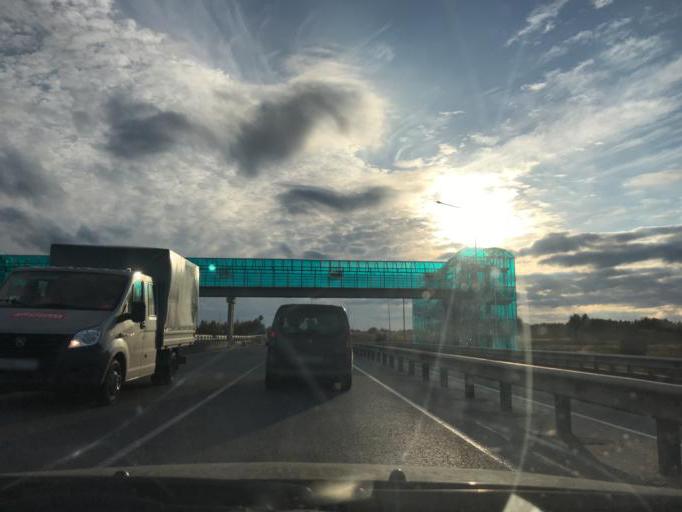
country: RU
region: Kaluga
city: Kurovskoye
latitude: 54.5399
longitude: 36.0059
